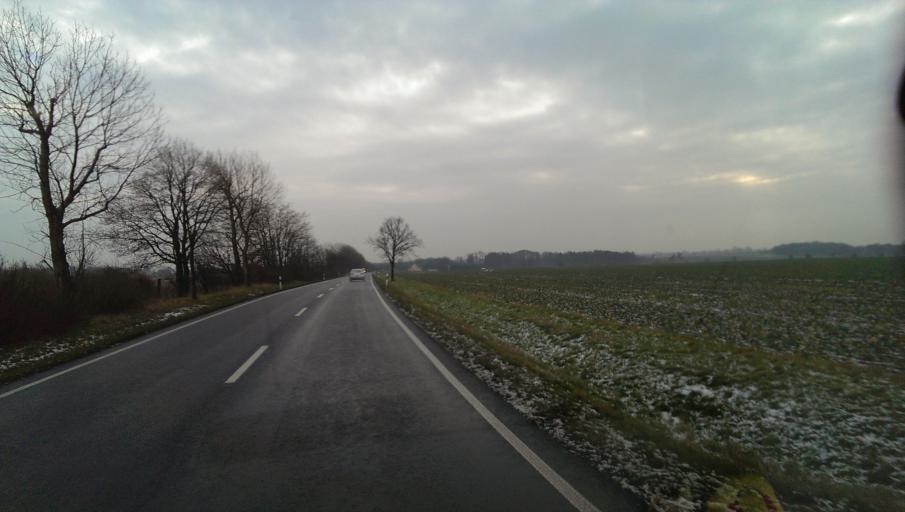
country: DE
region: Saxony
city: Zabeltitz
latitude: 51.3498
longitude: 13.5346
